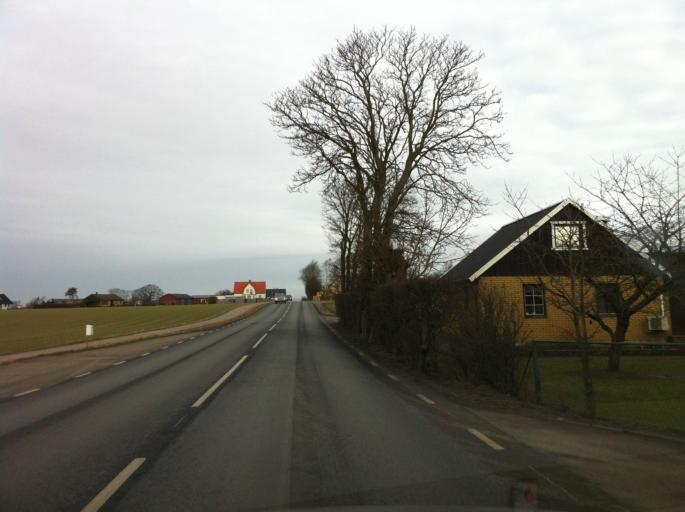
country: SE
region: Skane
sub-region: Angelholms Kommun
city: AEngelholm
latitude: 56.2015
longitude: 12.8541
